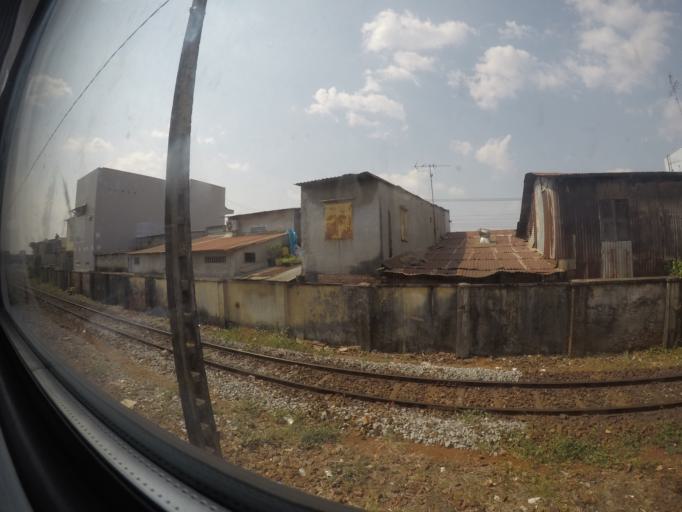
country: VN
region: Dong Nai
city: Long Khanh
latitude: 10.9338
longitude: 107.2459
